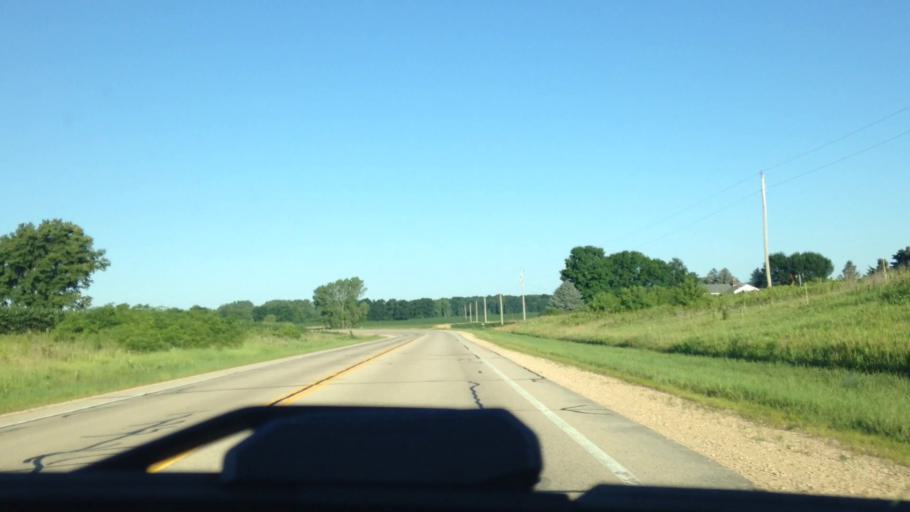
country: US
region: Wisconsin
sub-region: Columbia County
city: Rio
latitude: 43.3402
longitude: -89.2500
